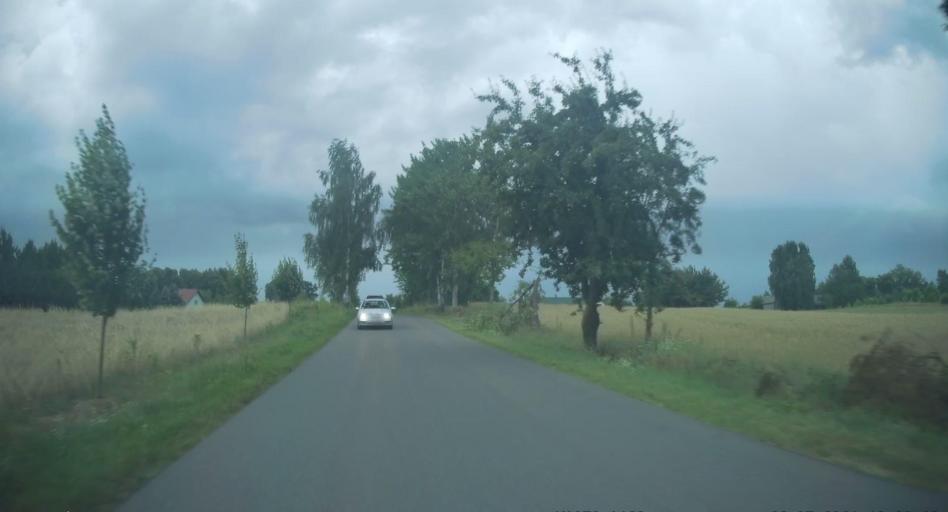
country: PL
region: Lodz Voivodeship
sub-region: Powiat rawski
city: Rawa Mazowiecka
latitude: 51.7473
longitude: 20.2108
